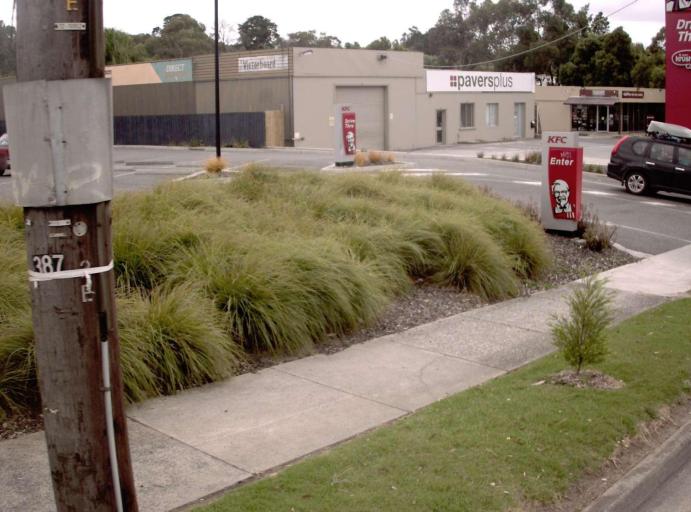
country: AU
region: Victoria
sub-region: Maroondah
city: Ringwood East
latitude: -37.8045
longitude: 145.2453
